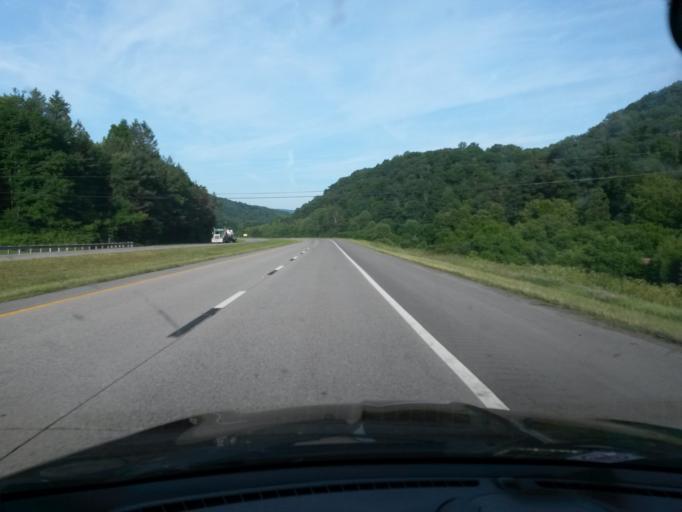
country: US
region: West Virginia
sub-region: Summers County
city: Hinton
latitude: 37.8009
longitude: -80.8372
